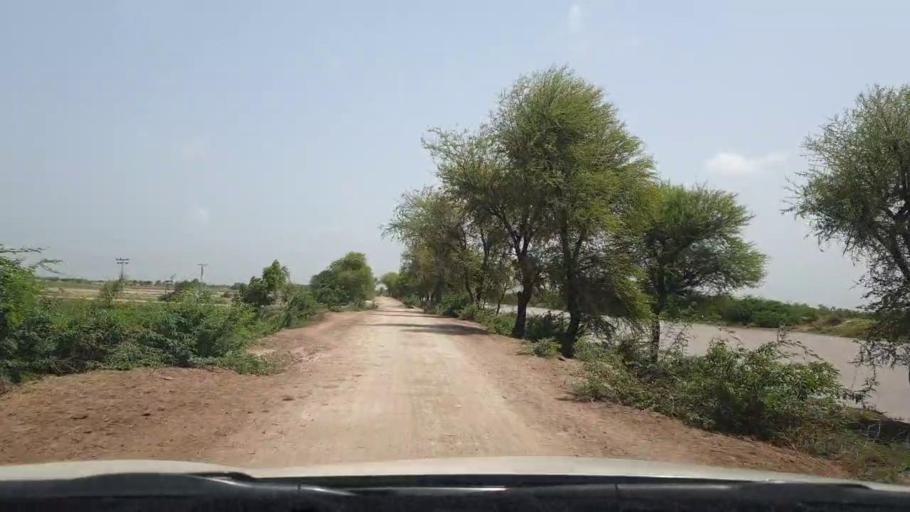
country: PK
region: Sindh
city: Talhar
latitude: 24.9218
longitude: 68.8397
